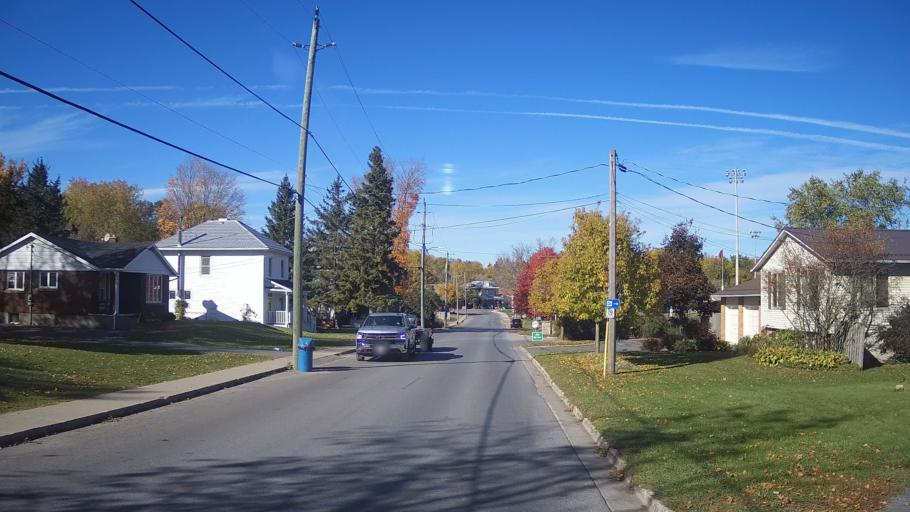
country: CA
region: Ontario
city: Kingston
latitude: 44.4097
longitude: -76.5950
